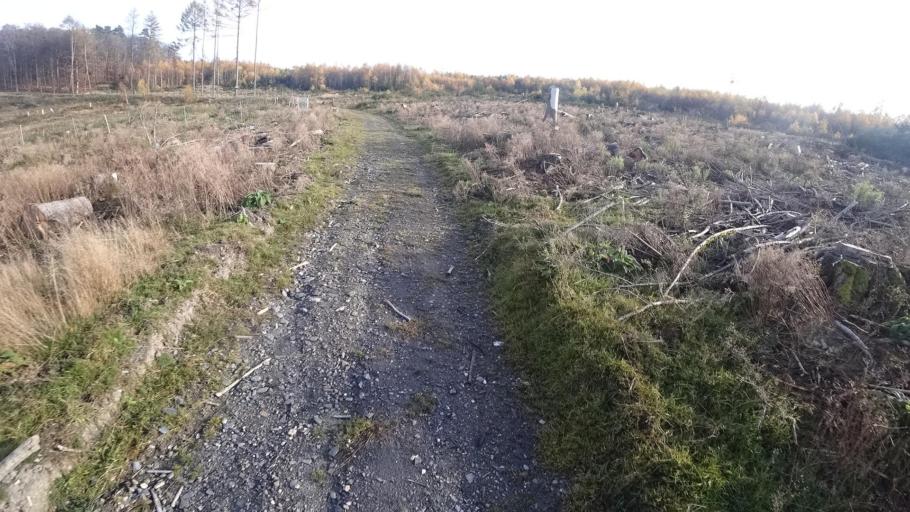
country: DE
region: Rheinland-Pfalz
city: Hungenroth
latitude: 50.1283
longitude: 7.6091
